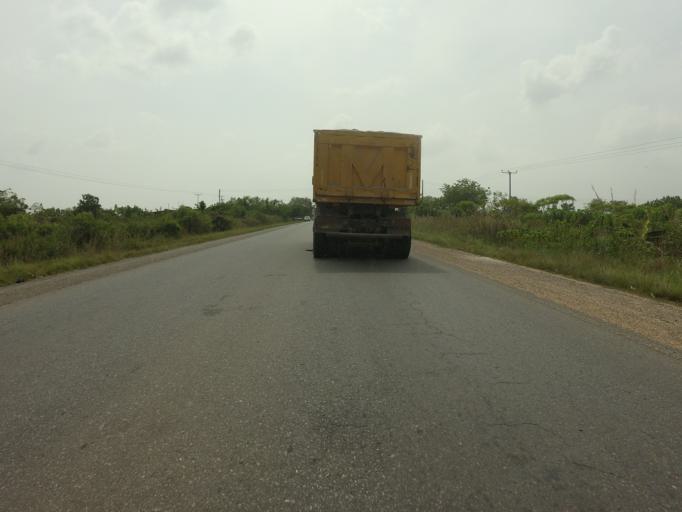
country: GH
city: Akropong
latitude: 6.0371
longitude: 0.0472
